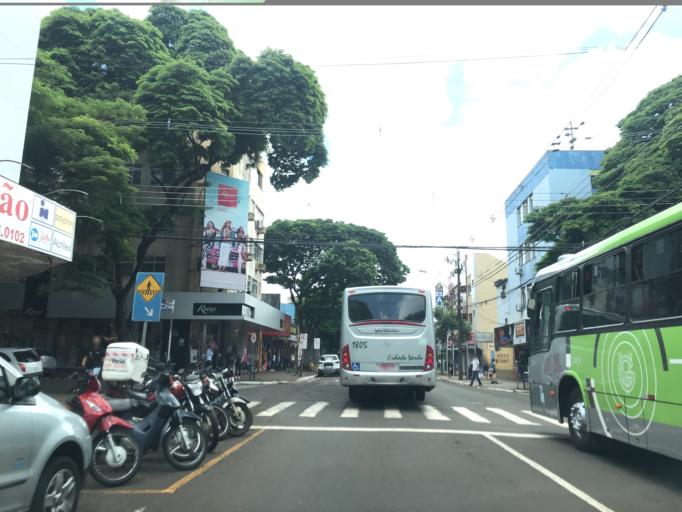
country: BR
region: Parana
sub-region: Maringa
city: Maringa
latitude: -23.4198
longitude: -51.9351
